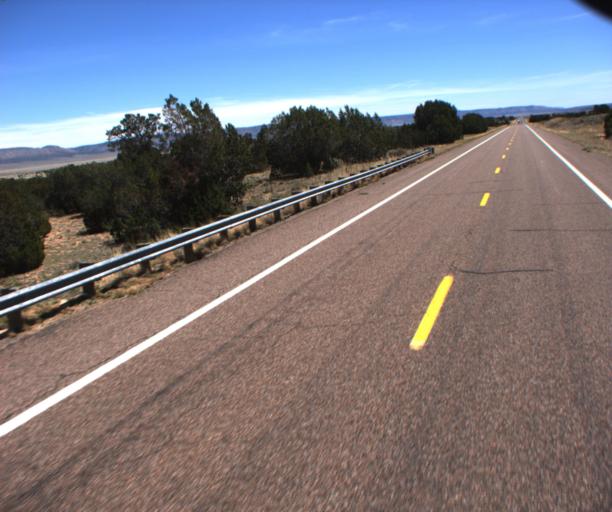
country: US
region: Arizona
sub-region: Mohave County
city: Peach Springs
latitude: 35.5105
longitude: -113.1882
